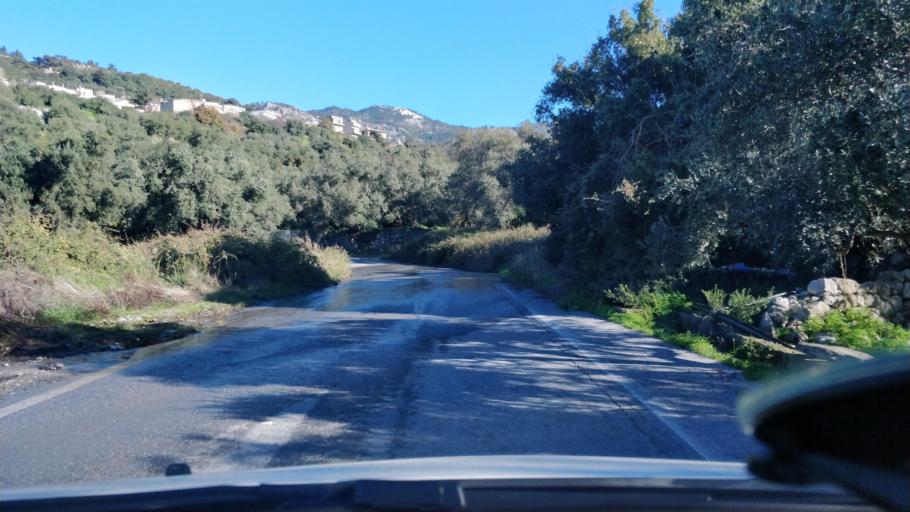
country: GR
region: Crete
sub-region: Nomos Lasithiou
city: Kritsa
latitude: 35.0764
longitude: 25.5843
